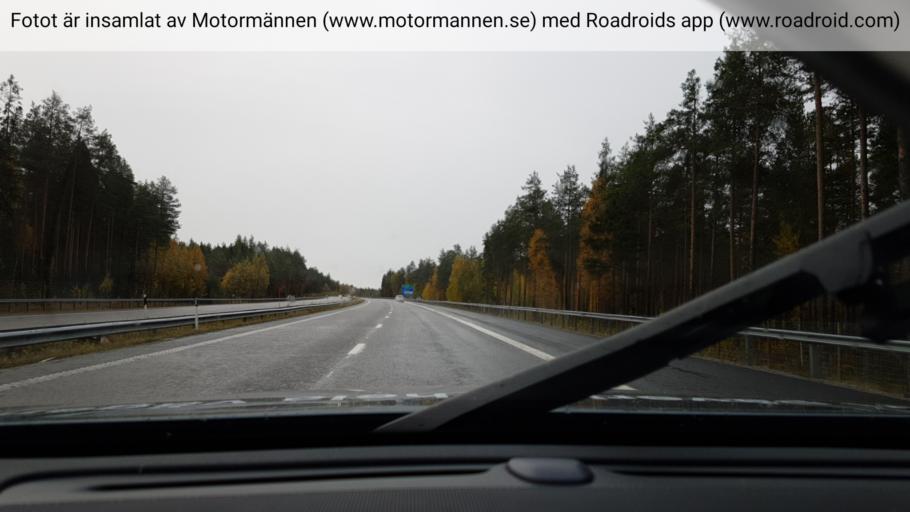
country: SE
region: Norrbotten
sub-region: Pitea Kommun
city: Pitea
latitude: 65.3422
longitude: 21.4378
